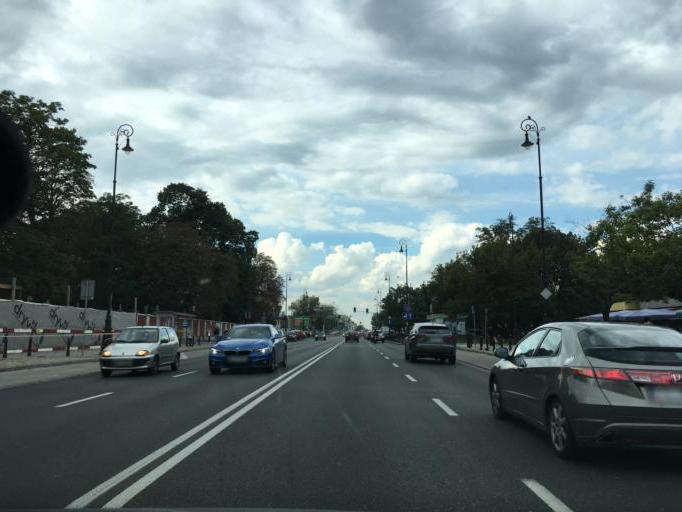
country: PL
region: Masovian Voivodeship
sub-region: Warszawa
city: Zoliborz
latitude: 52.2541
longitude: 20.9748
